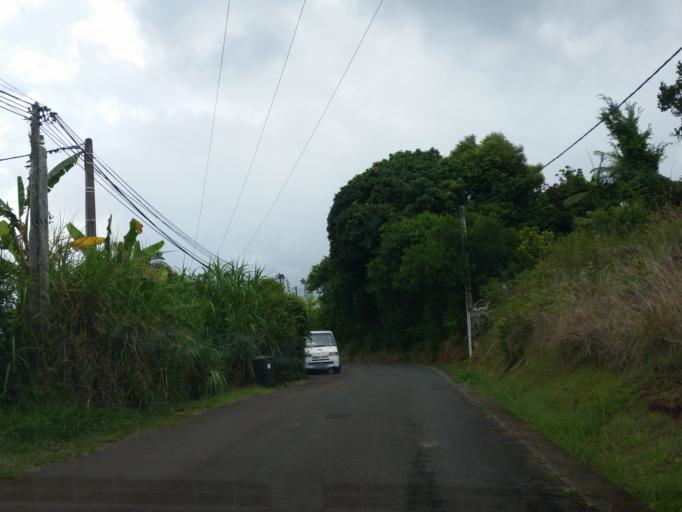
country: RE
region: Reunion
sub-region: Reunion
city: L'Entre-Deux
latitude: -21.2447
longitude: 55.4797
